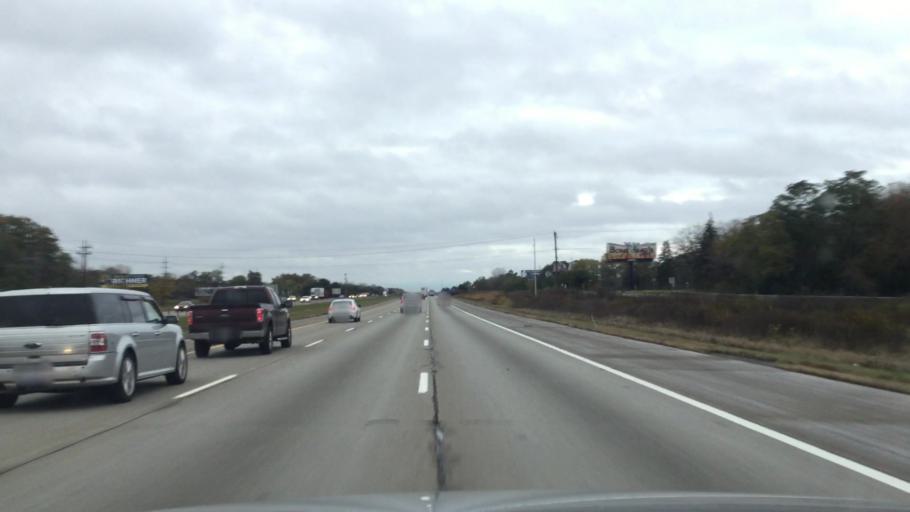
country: US
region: Michigan
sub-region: Wayne County
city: Belleville
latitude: 42.2195
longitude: -83.5016
